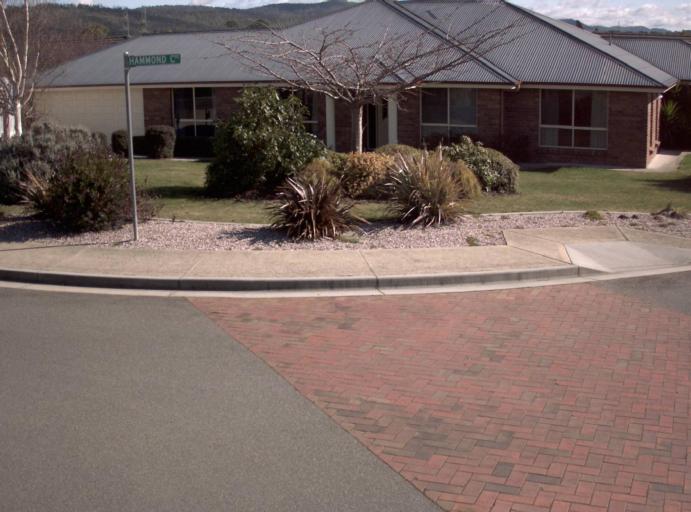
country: AU
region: Tasmania
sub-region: Launceston
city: Summerhill
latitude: -41.4738
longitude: 147.1145
